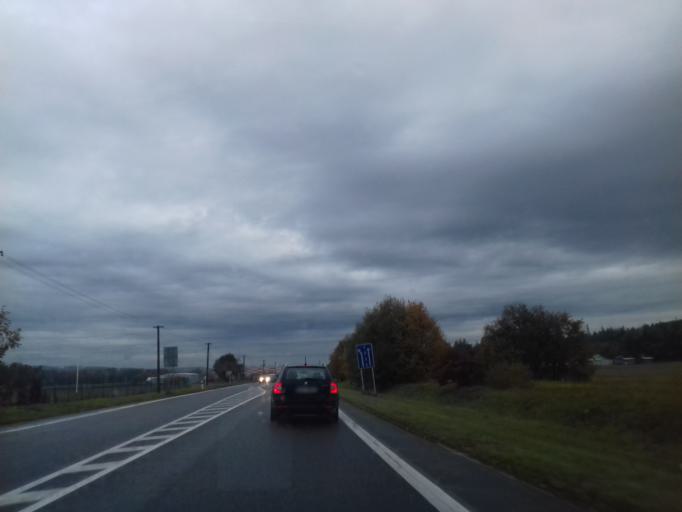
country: CZ
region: Pardubicky
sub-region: Okres Pardubice
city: Vysoke Myto
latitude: 49.9296
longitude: 16.1784
